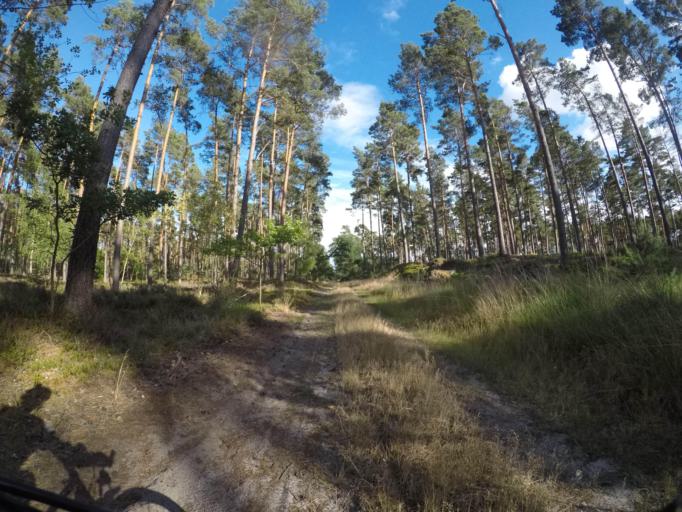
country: DE
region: Mecklenburg-Vorpommern
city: Lubtheen
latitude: 53.2573
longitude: 10.9949
